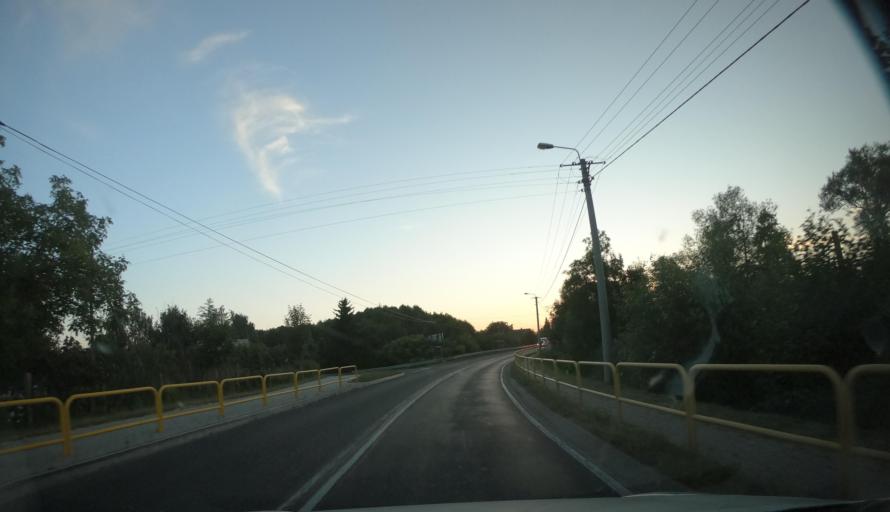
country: PL
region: Kujawsko-Pomorskie
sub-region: Powiat bydgoski
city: Koronowo
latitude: 53.3282
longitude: 17.9002
